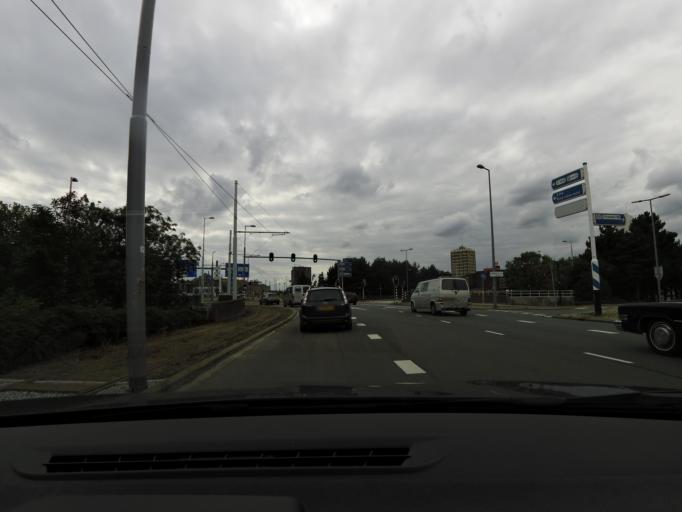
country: NL
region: South Holland
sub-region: Gemeente Rotterdam
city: Delfshaven
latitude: 51.9084
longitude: 4.4665
